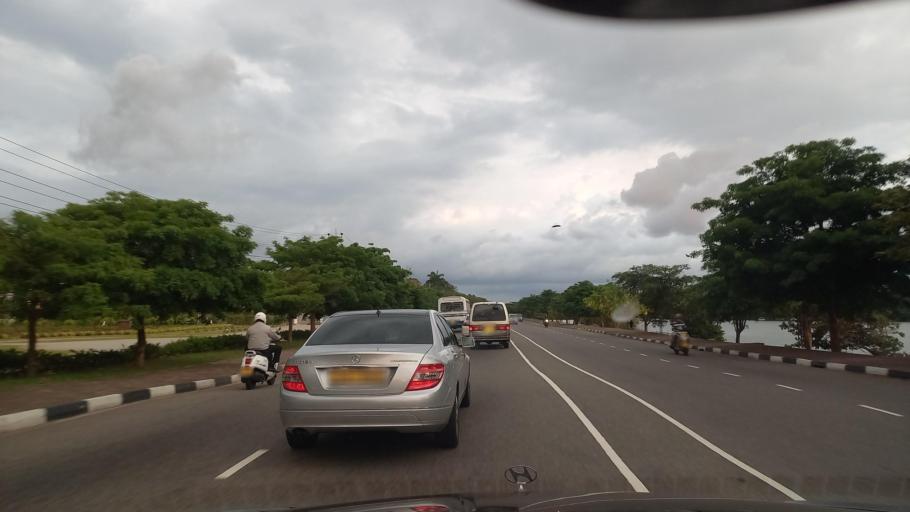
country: LK
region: Western
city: Battaramulla South
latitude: 6.8877
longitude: 79.9223
